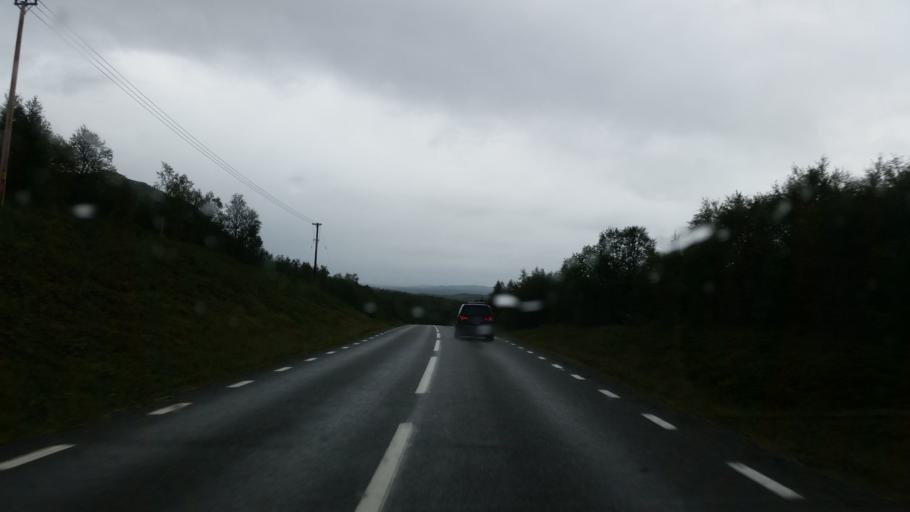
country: NO
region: Nordland
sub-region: Rana
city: Mo i Rana
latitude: 65.9088
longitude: 14.9885
